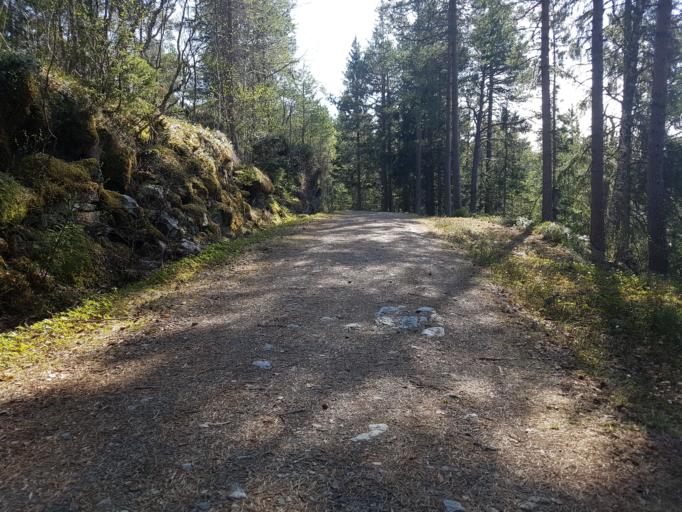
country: NO
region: Sor-Trondelag
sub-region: Trondheim
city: Trondheim
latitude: 63.4346
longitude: 10.2917
